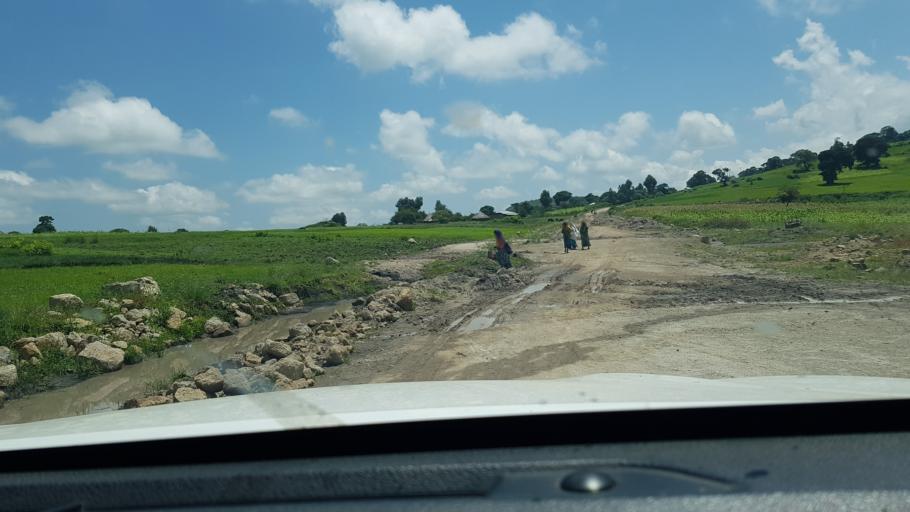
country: ET
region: Oromiya
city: Sirre
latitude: 8.4388
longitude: 39.8796
